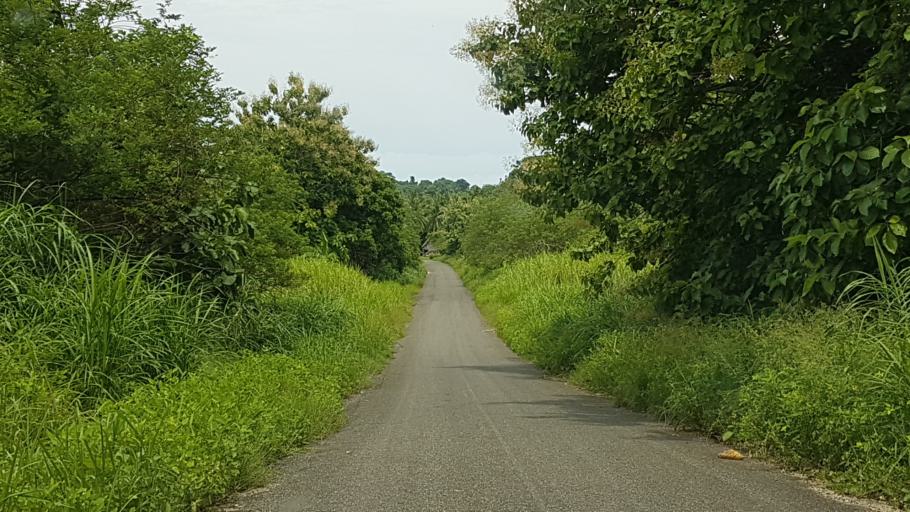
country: PG
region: Madang
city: Madang
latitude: -4.6106
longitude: 145.5544
